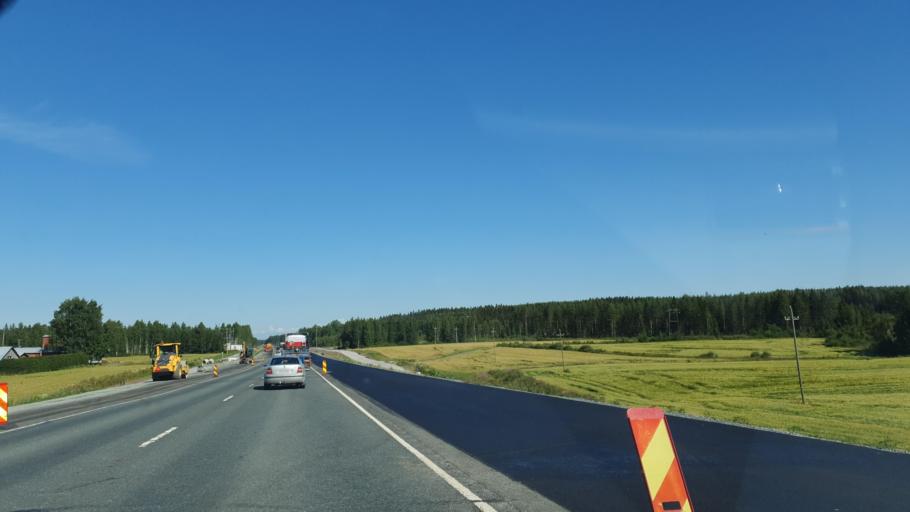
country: FI
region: Northern Savo
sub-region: Ylae-Savo
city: Lapinlahti
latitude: 63.2857
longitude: 27.4551
